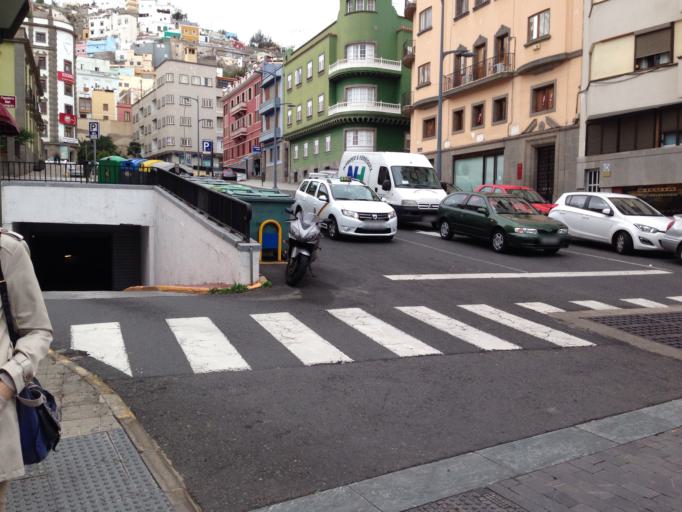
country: ES
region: Canary Islands
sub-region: Provincia de Las Palmas
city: Las Palmas de Gran Canaria
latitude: 28.1052
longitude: -15.4183
